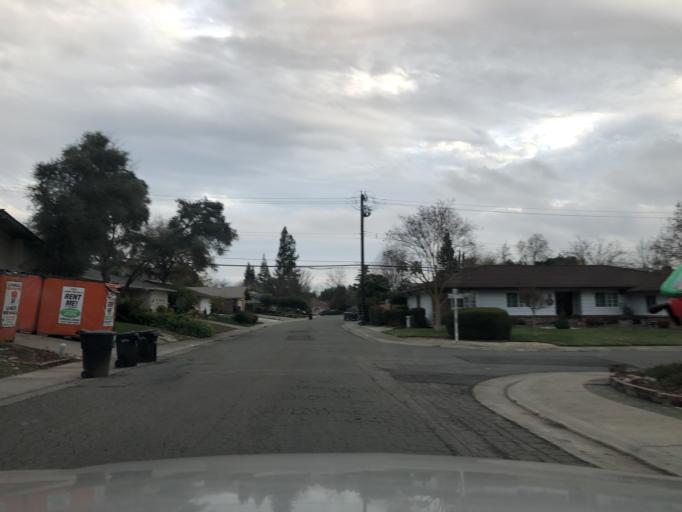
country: US
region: California
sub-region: Sacramento County
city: Foothill Farms
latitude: 38.6592
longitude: -121.3134
